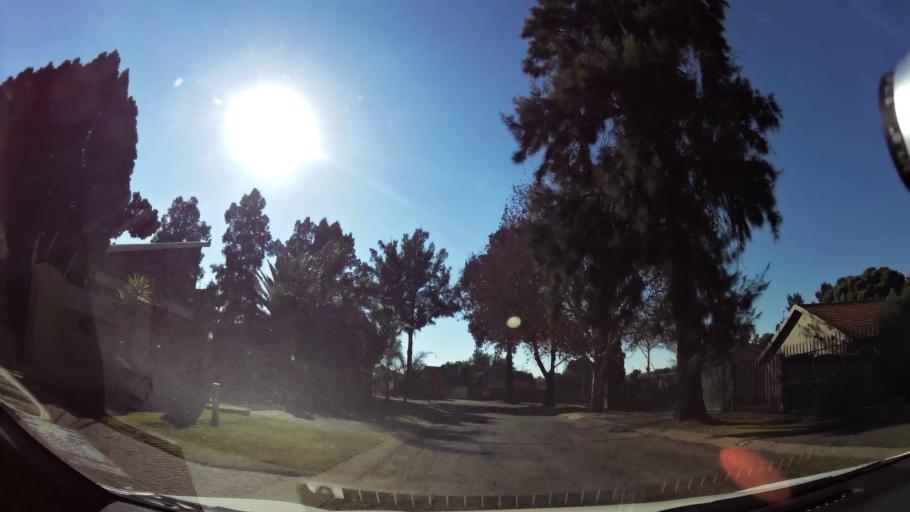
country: ZA
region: Gauteng
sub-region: Ekurhuleni Metropolitan Municipality
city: Germiston
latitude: -26.3376
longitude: 28.1025
